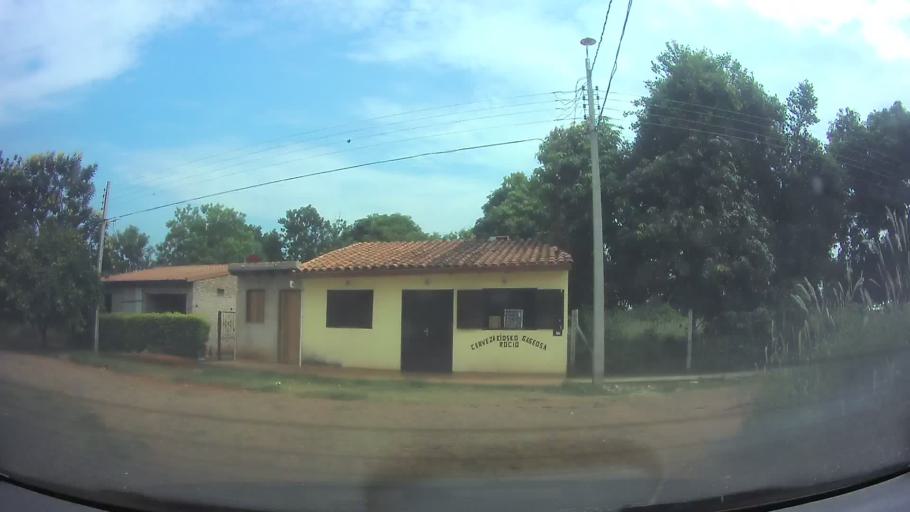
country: PY
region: Central
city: San Lorenzo
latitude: -25.2909
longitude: -57.5069
